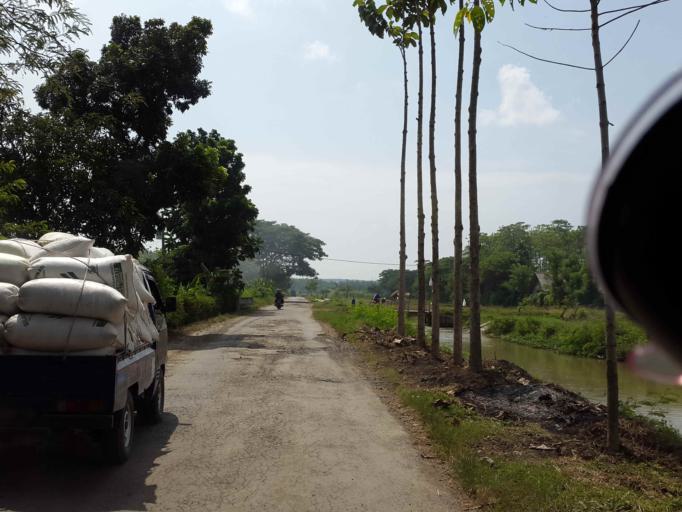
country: ID
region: Central Java
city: Pemalang
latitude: -6.9498
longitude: 109.3541
